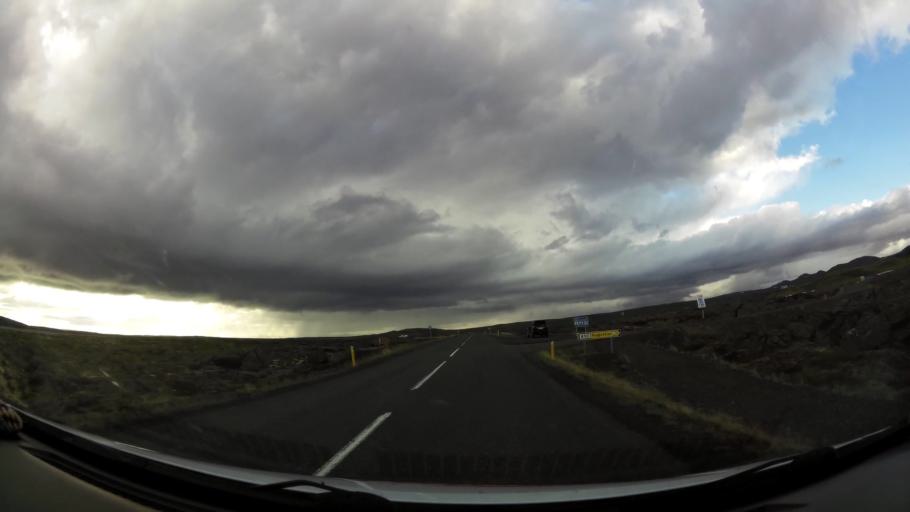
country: IS
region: Northeast
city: Laugar
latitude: 65.6460
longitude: -16.9207
